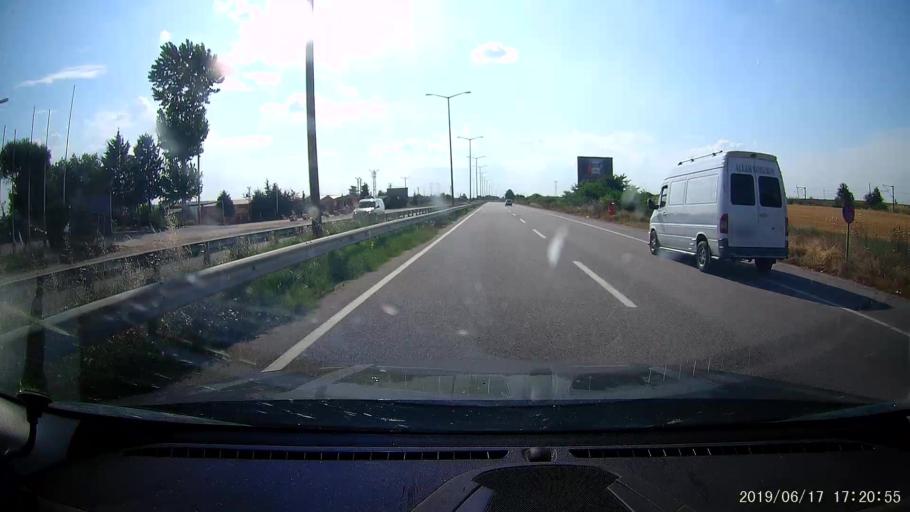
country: GR
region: East Macedonia and Thrace
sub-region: Nomos Evrou
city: Rizia
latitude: 41.7036
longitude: 26.4049
